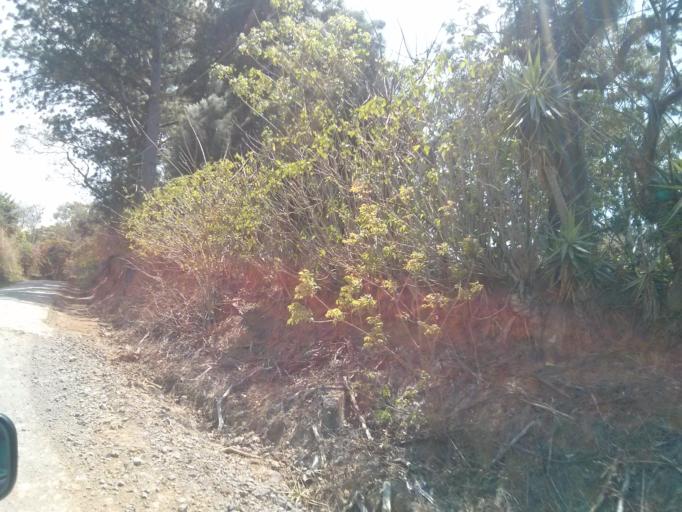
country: CR
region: Heredia
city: Colon
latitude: 9.9164
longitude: -84.2164
